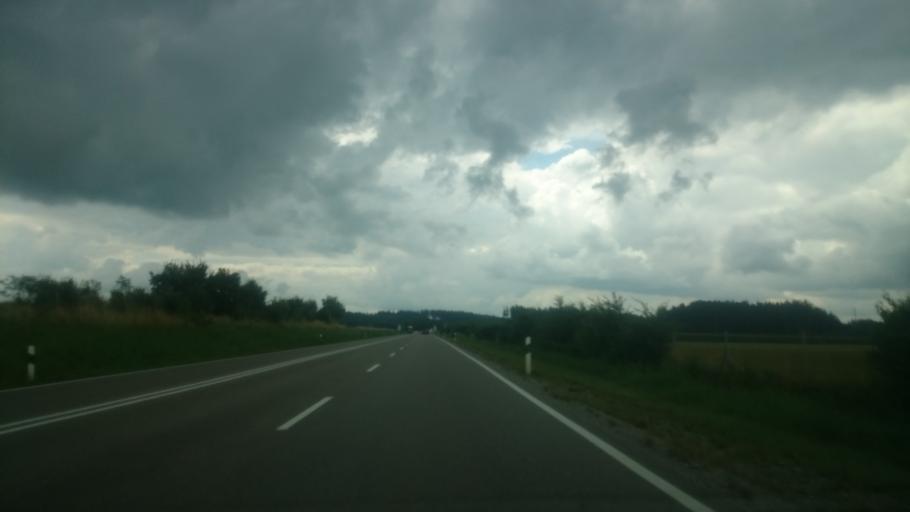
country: DE
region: Bavaria
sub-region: Swabia
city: Rieden
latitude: 47.9204
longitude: 10.6587
